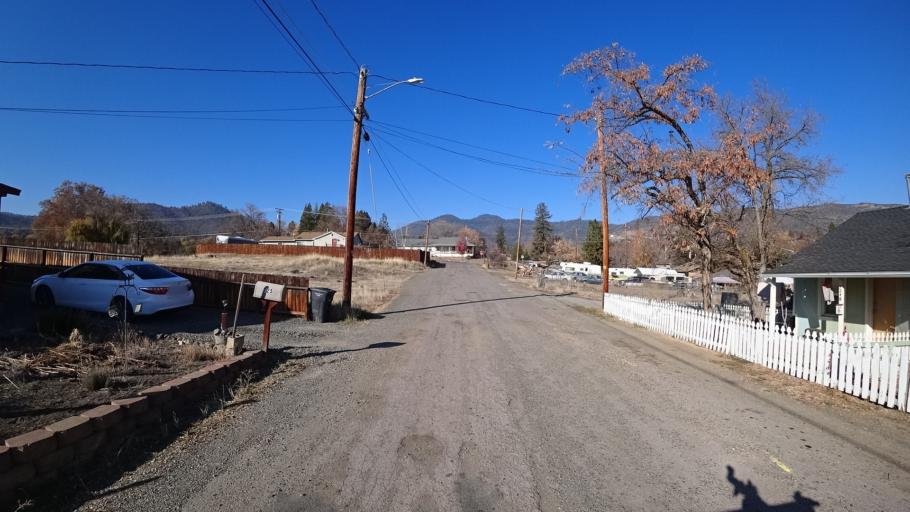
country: US
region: California
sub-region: Siskiyou County
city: Yreka
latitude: 41.7328
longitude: -122.6451
